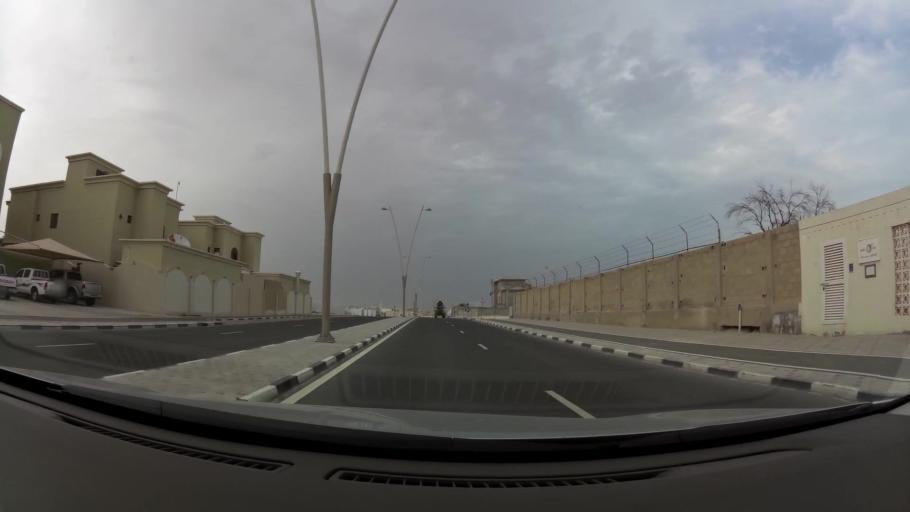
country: QA
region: Baladiyat ad Dawhah
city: Doha
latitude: 25.3404
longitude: 51.4945
